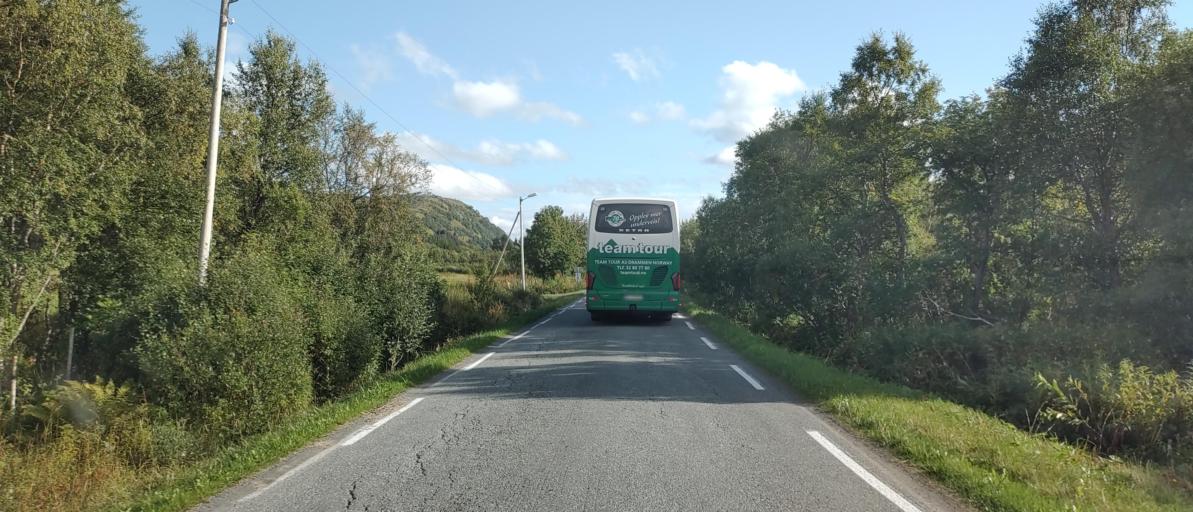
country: NO
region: Nordland
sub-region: Sortland
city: Sortland
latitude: 69.0355
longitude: 15.5237
